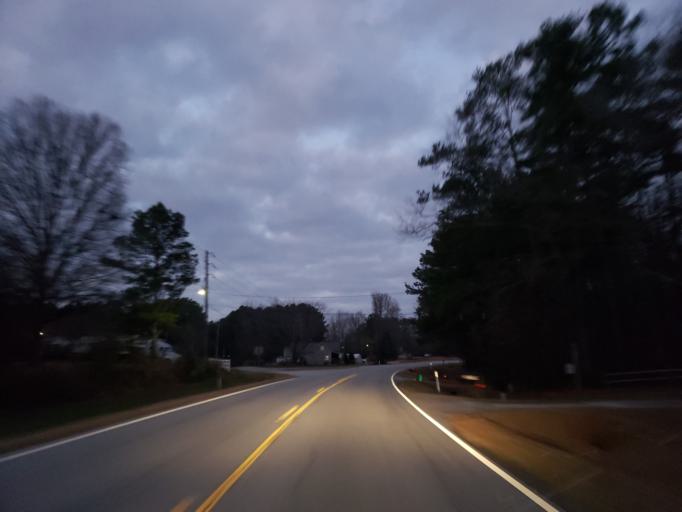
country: US
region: Georgia
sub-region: Carroll County
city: Temple
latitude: 33.8047
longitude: -85.0561
